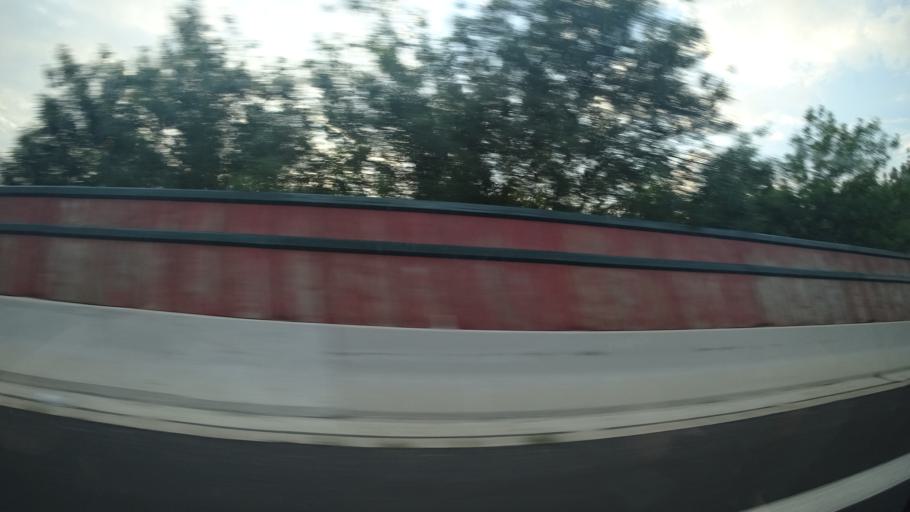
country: FR
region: Languedoc-Roussillon
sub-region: Departement de l'Herault
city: Pezenas
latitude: 43.4717
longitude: 3.4351
